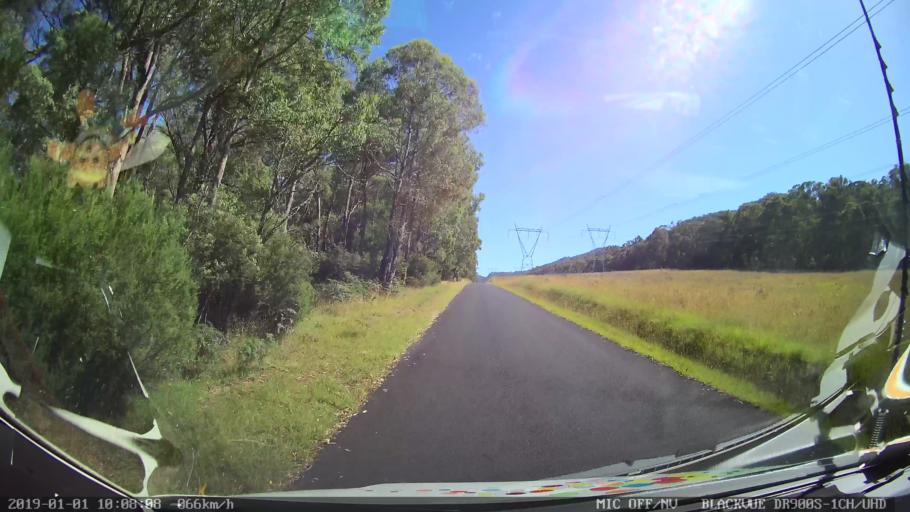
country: AU
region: New South Wales
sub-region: Snowy River
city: Jindabyne
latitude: -36.1623
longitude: 148.1573
